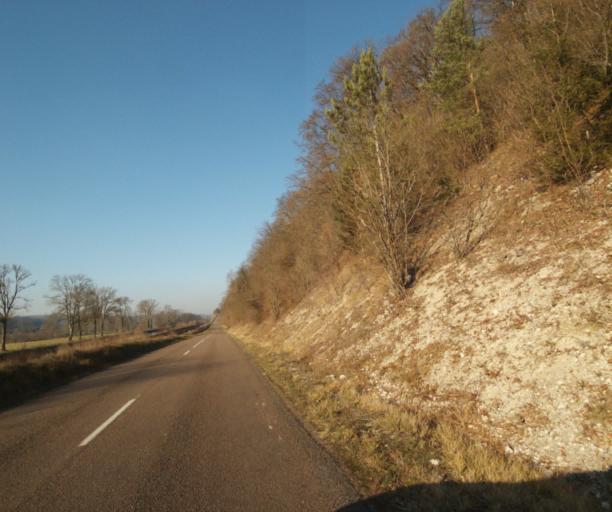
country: FR
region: Champagne-Ardenne
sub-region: Departement de la Haute-Marne
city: Chevillon
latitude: 48.5094
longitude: 5.1226
